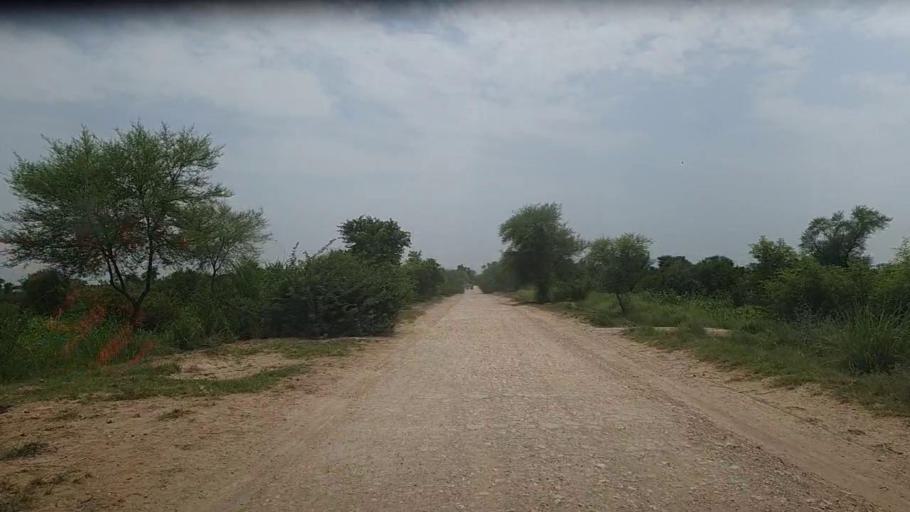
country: PK
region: Sindh
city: Bhiria
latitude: 26.8919
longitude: 68.2979
